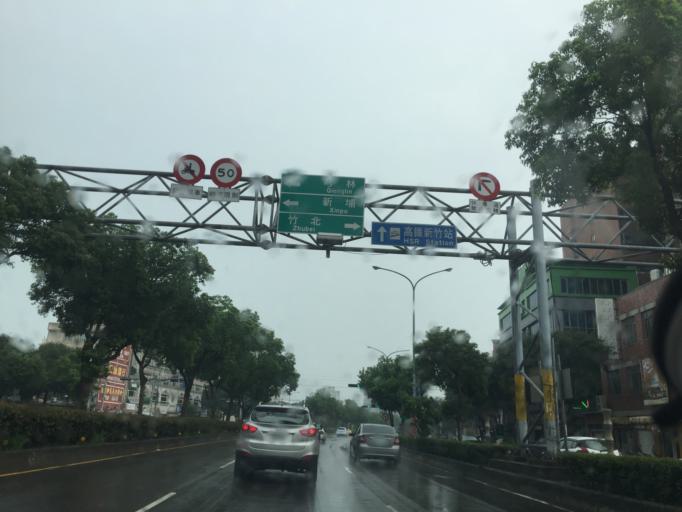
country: TW
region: Taiwan
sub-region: Hsinchu
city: Zhubei
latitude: 24.8195
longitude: 121.0288
